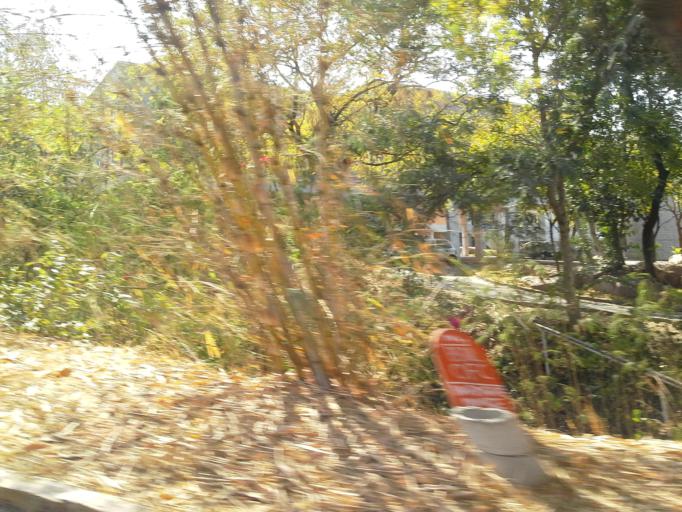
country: IN
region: Telangana
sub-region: Hyderabad
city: Hyderabad
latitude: 17.3090
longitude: 78.4130
